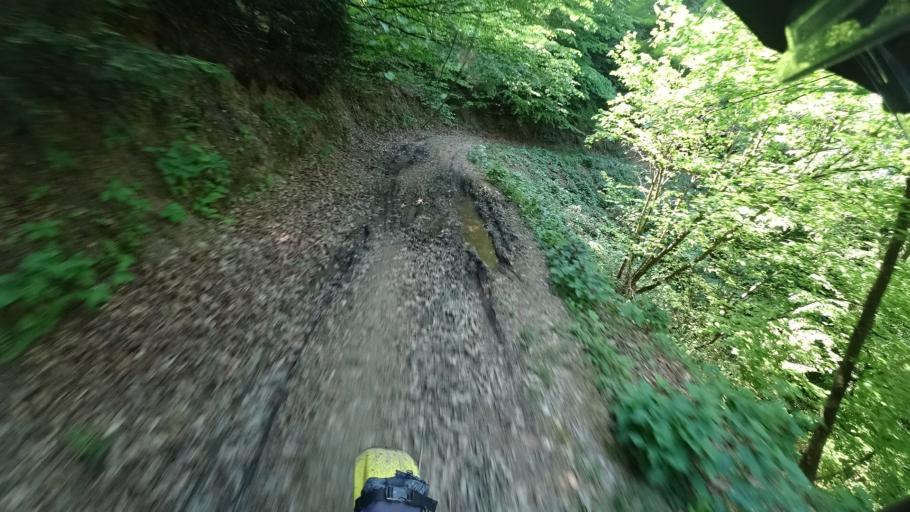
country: HR
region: Grad Zagreb
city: Kasina
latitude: 45.9472
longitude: 15.9741
